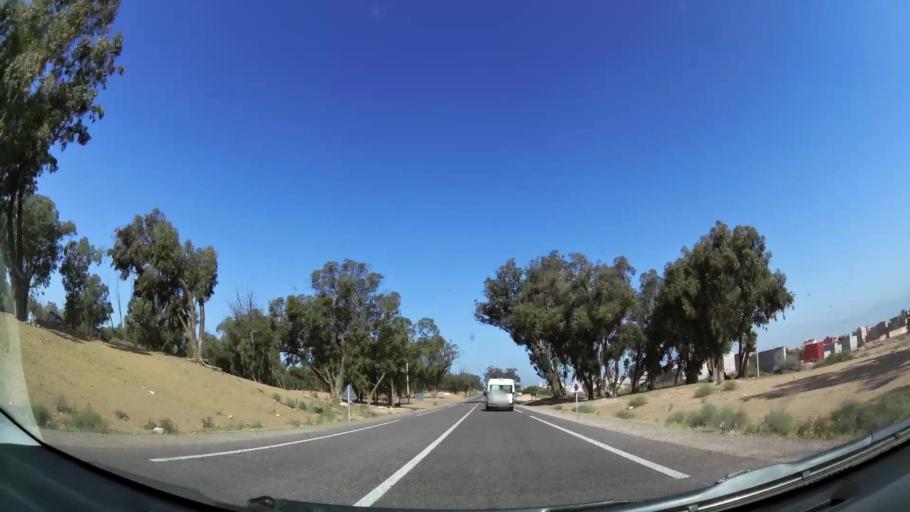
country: MA
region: Souss-Massa-Draa
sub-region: Inezgane-Ait Mellou
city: Inezgane
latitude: 30.3223
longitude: -9.5294
